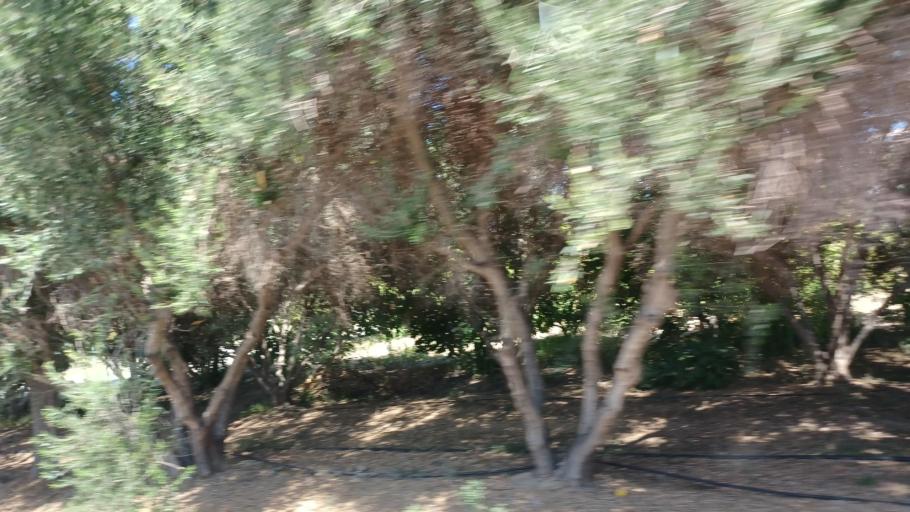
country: CY
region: Pafos
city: Polis
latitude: 35.0450
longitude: 32.4332
